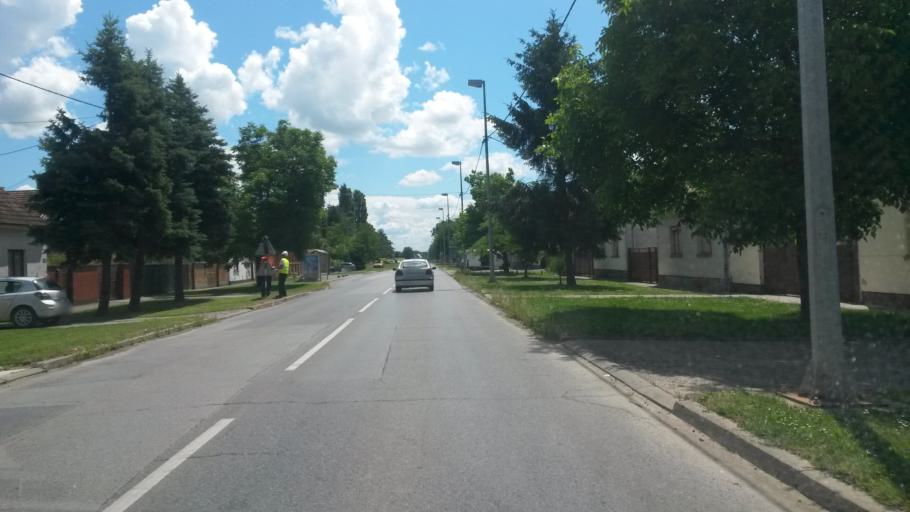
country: HR
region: Osjecko-Baranjska
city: Viskovci
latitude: 45.3304
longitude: 18.4192
